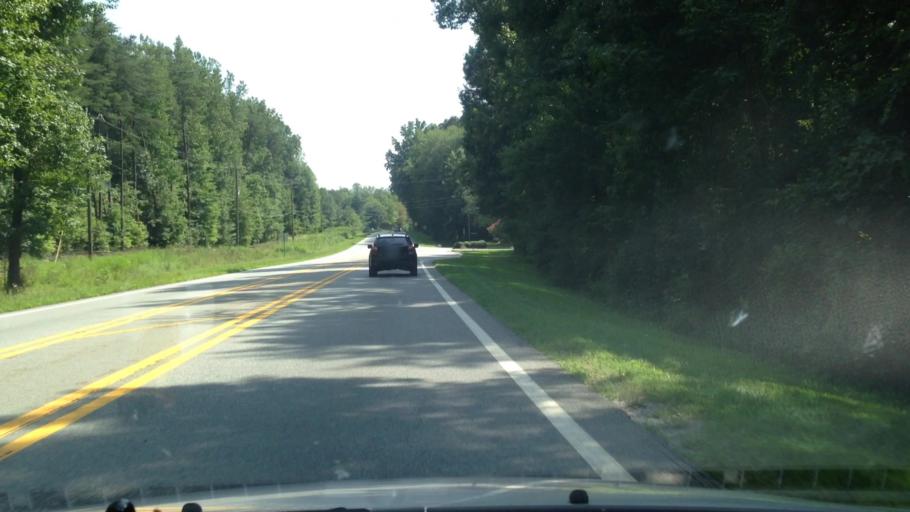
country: US
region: North Carolina
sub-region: Guilford County
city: Oak Ridge
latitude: 36.1882
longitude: -79.9859
